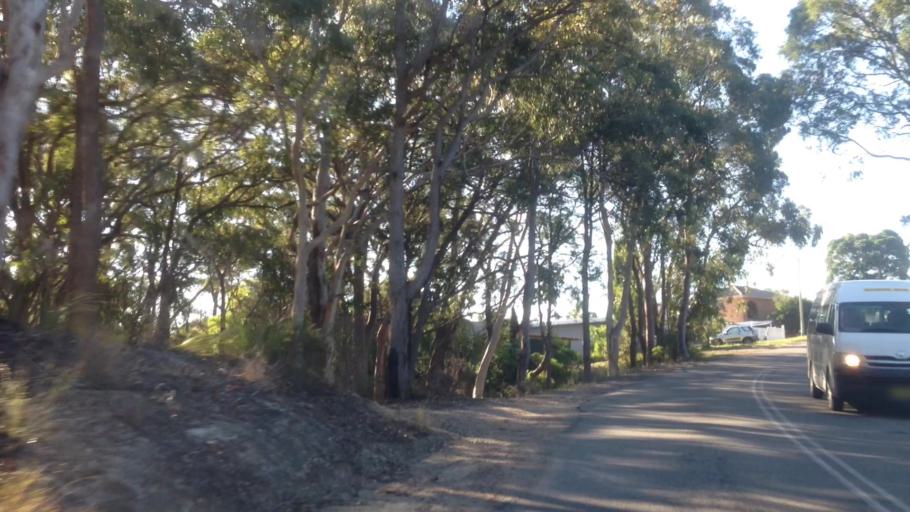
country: AU
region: New South Wales
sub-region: Lake Macquarie Shire
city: Arcadia vale
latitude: -33.1092
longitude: 151.5590
